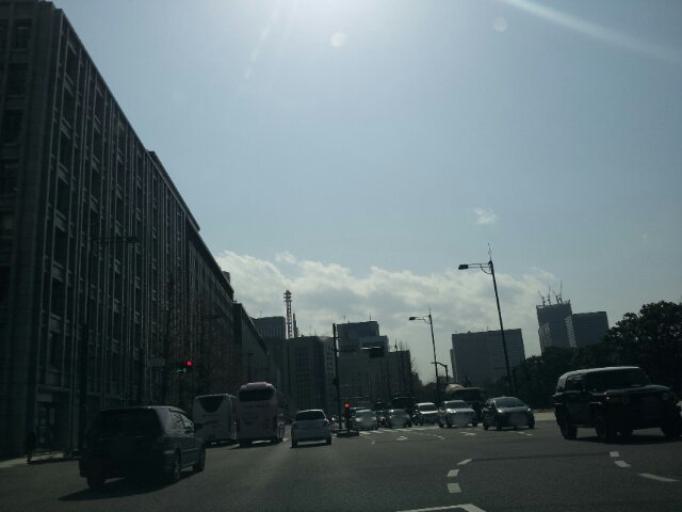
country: JP
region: Tokyo
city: Tokyo
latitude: 35.6788
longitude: 139.7608
